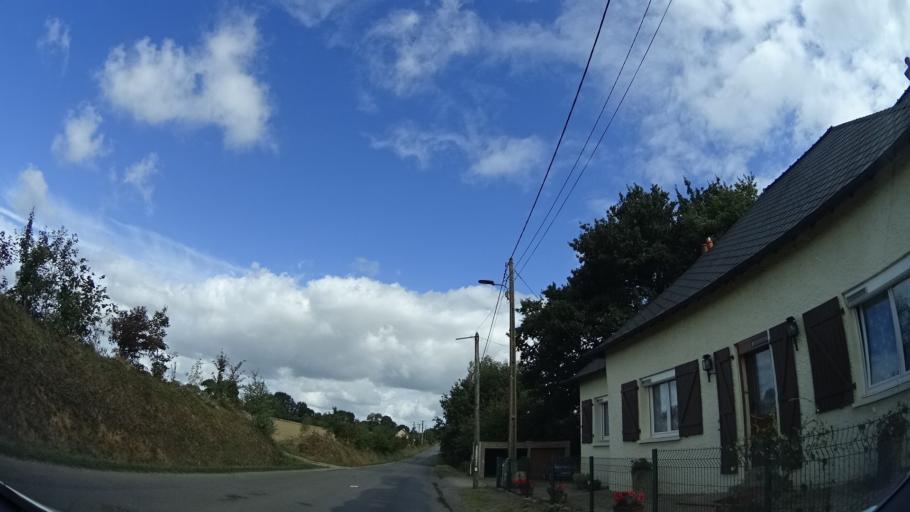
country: FR
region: Brittany
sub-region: Departement d'Ille-et-Vilaine
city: Montreuil-sur-Ille
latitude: 48.3123
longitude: -1.6788
